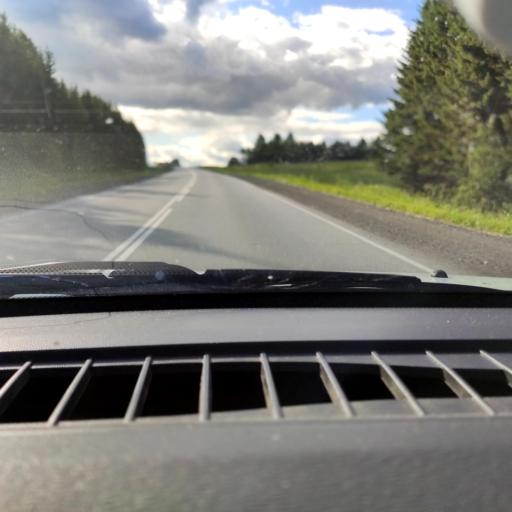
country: RU
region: Perm
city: Kungur
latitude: 57.4740
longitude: 56.7416
